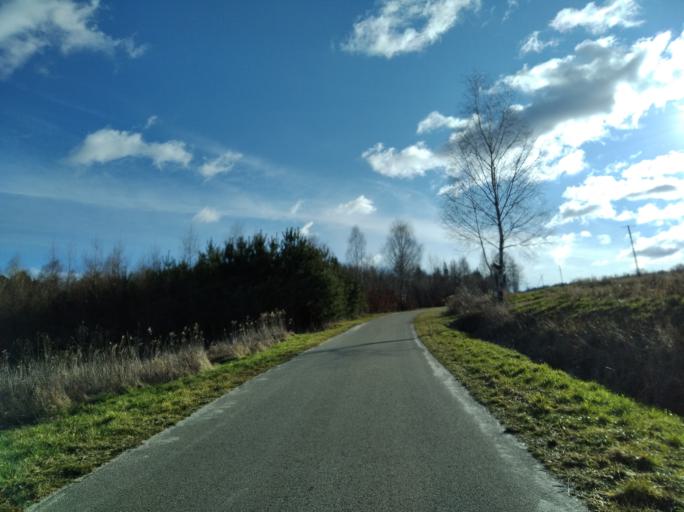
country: PL
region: Subcarpathian Voivodeship
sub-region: Powiat strzyzowski
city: Wisniowa
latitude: 49.9007
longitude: 21.6868
